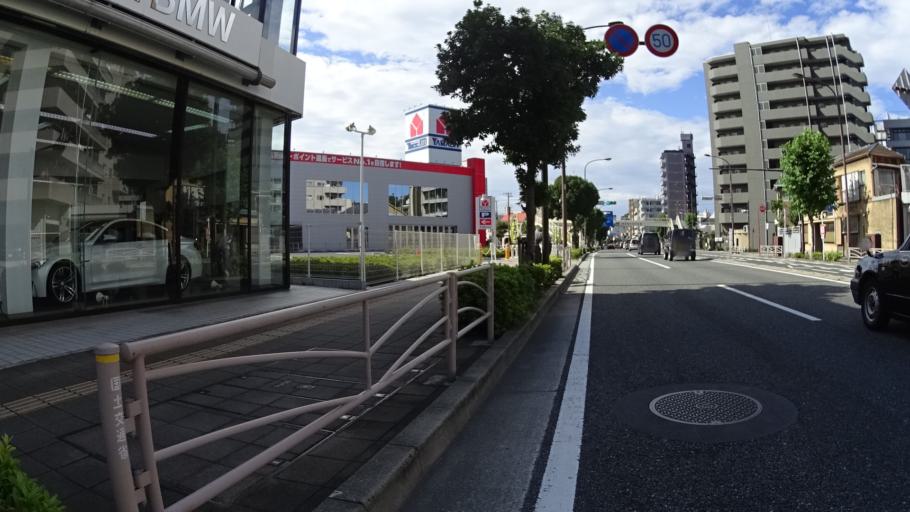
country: JP
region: Kanagawa
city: Yokosuka
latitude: 35.2768
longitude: 139.6771
